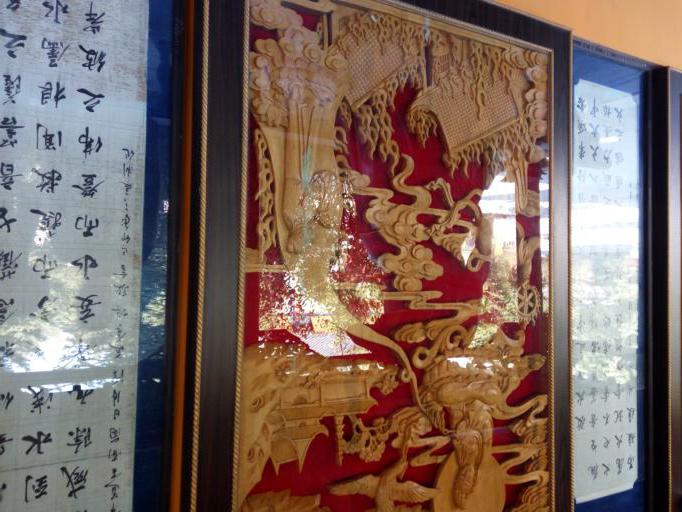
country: CN
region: Heilongjiang Sheng
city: Erjing
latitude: 48.6502
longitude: 126.1268
